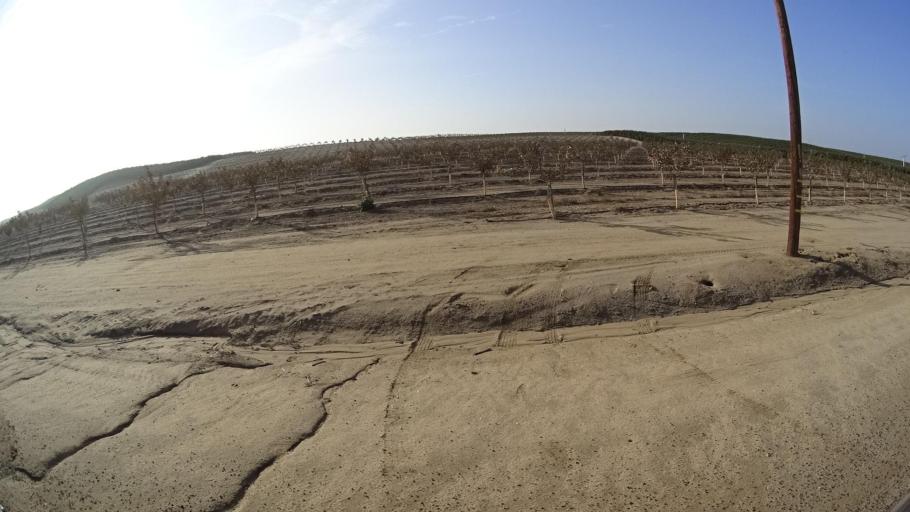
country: US
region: California
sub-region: Kern County
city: McFarland
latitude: 35.6671
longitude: -119.1143
